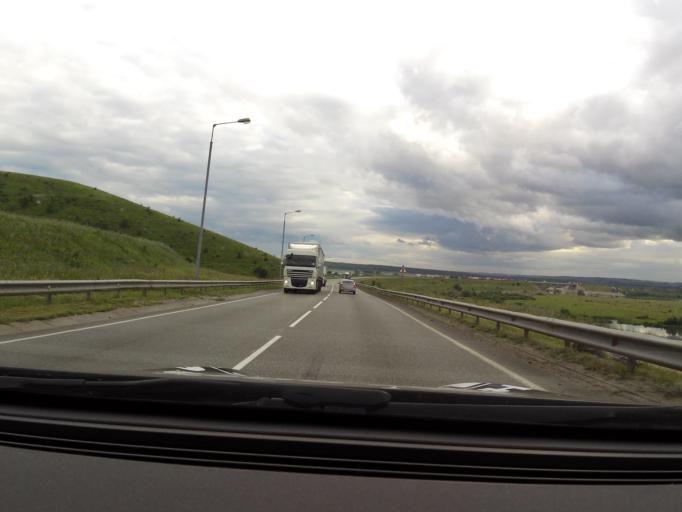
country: RU
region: Tatarstan
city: Sviyazhsk
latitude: 55.7209
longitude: 48.6103
